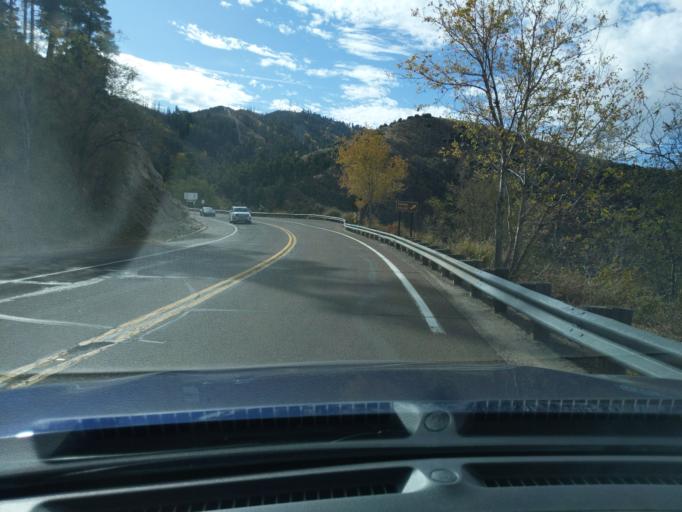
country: US
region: Arizona
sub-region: Pinal County
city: Oracle
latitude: 32.4482
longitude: -110.7552
